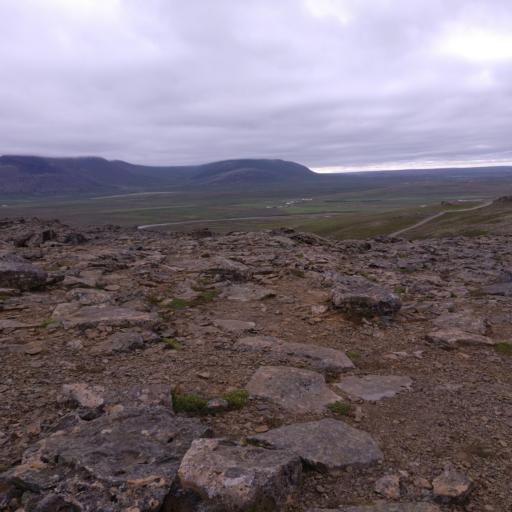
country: IS
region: Northwest
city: Saudarkrokur
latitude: 65.4750
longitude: -20.5980
